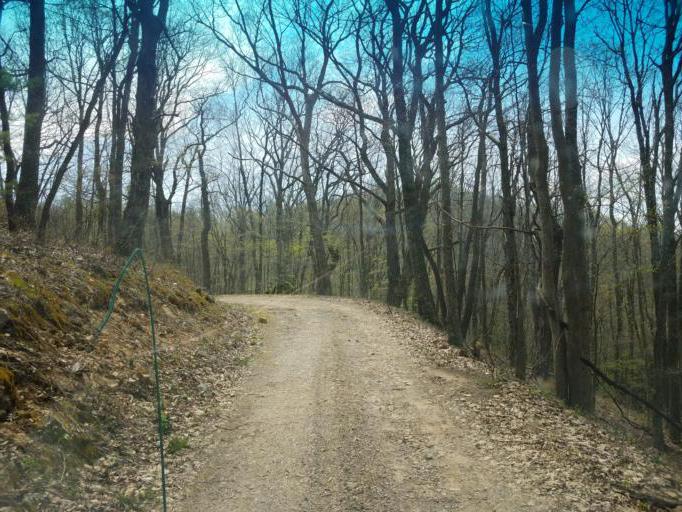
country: US
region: Virginia
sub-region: Smyth County
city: Marion
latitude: 36.7886
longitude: -81.4705
